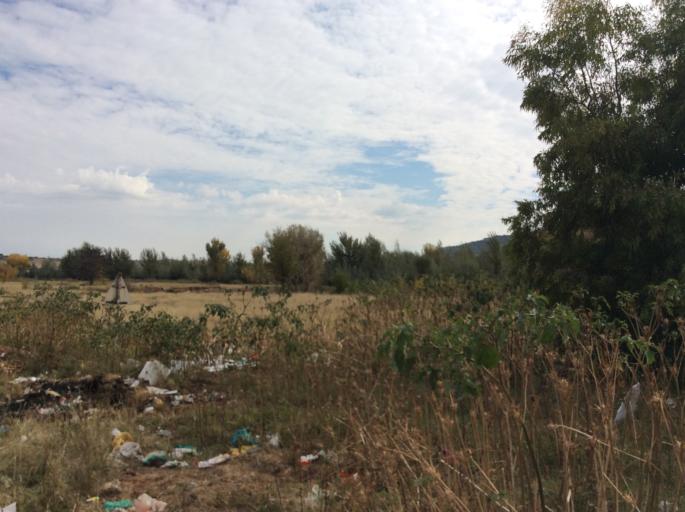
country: LS
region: Mafeteng
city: Mafeteng
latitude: -29.7281
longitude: 27.0281
